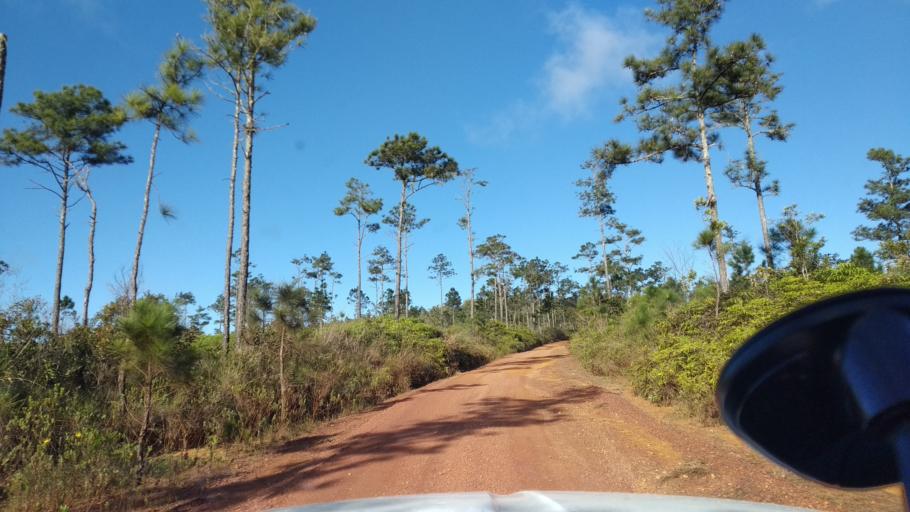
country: BZ
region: Cayo
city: Belmopan
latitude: 16.9974
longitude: -88.8437
